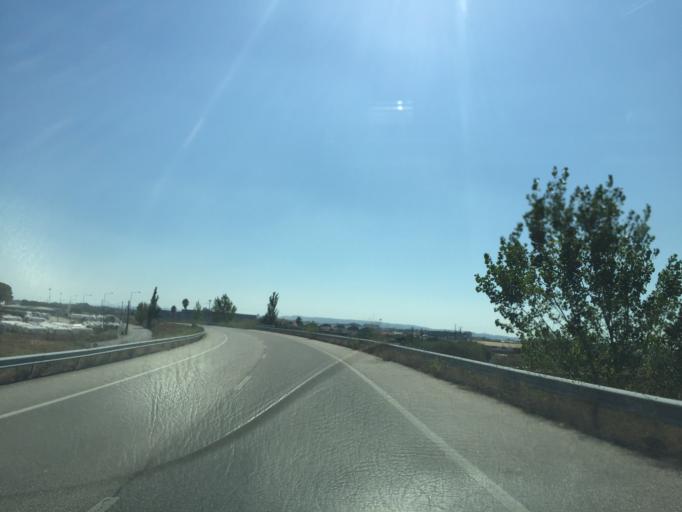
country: PT
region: Lisbon
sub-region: Azambuja
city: Aveiras de Cima
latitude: 39.1486
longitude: -8.8987
